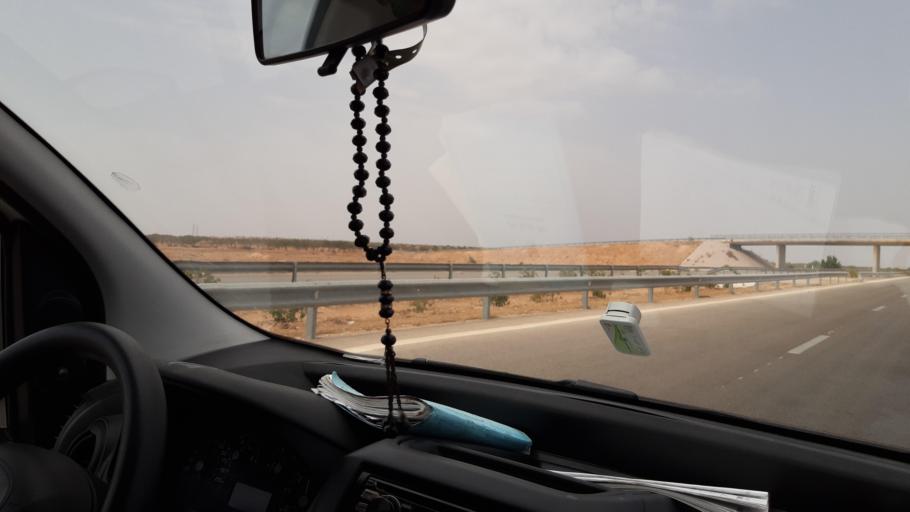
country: TN
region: Safaqis
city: Sfax
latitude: 34.8565
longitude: 10.6832
